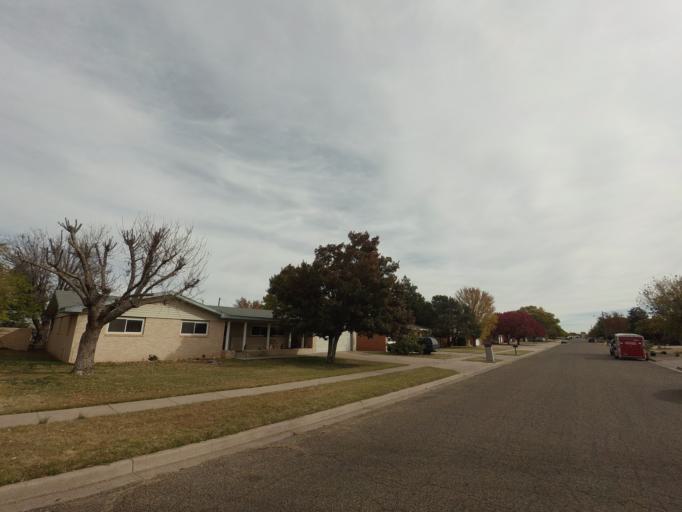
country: US
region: New Mexico
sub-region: Curry County
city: Clovis
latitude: 34.4222
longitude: -103.2137
